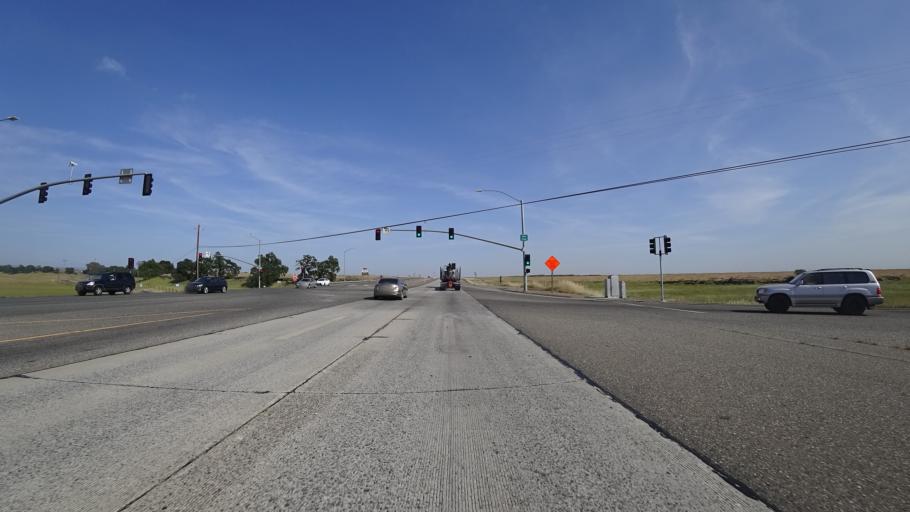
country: US
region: California
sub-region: Butte County
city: Durham
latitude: 39.6661
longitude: -121.7445
